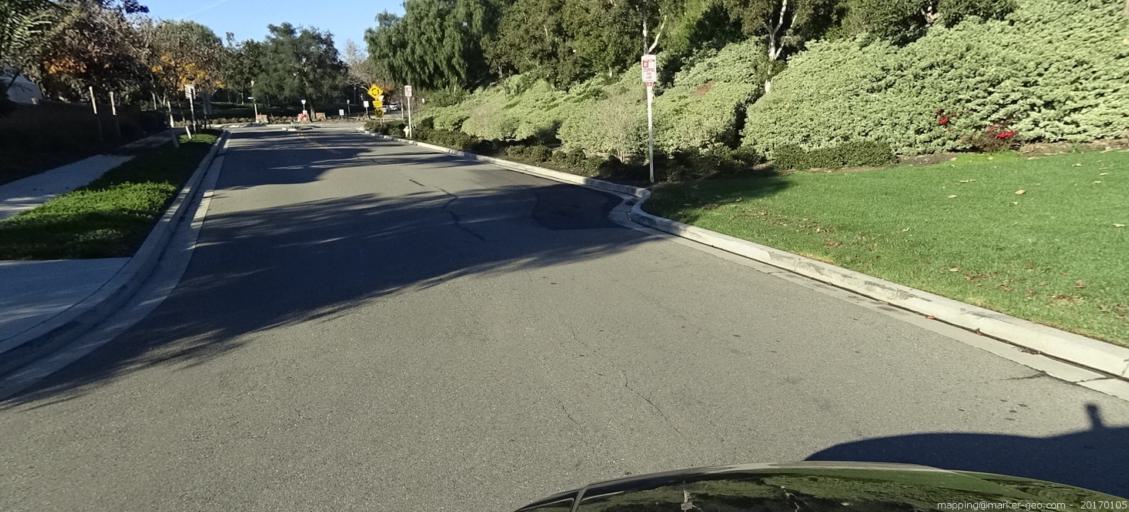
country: US
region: California
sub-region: Orange County
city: Ladera Ranch
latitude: 33.5367
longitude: -117.6433
